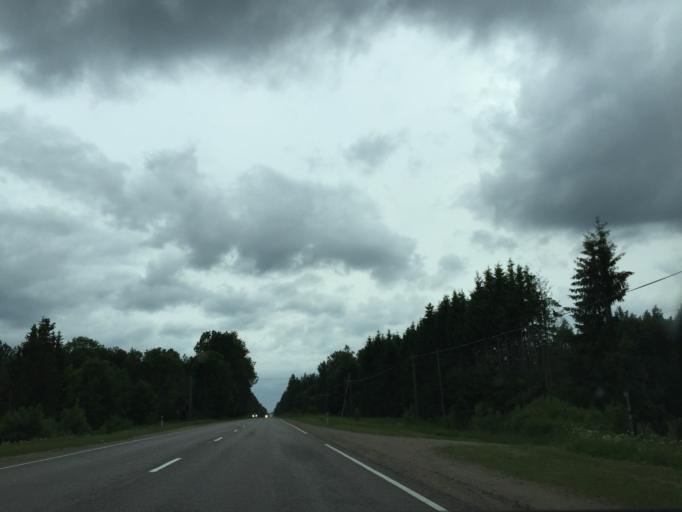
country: LV
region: Smiltene
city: Smiltene
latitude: 57.3970
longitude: 26.0103
